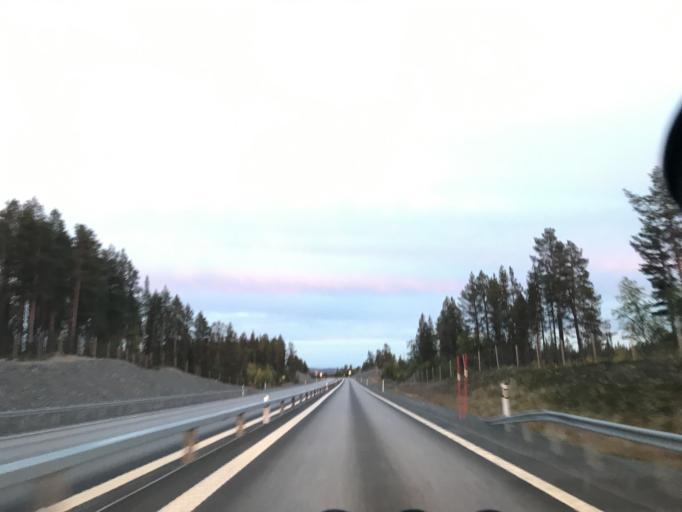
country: SE
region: Norrbotten
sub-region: Gallivare Kommun
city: Malmberget
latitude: 67.6794
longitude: 20.8812
